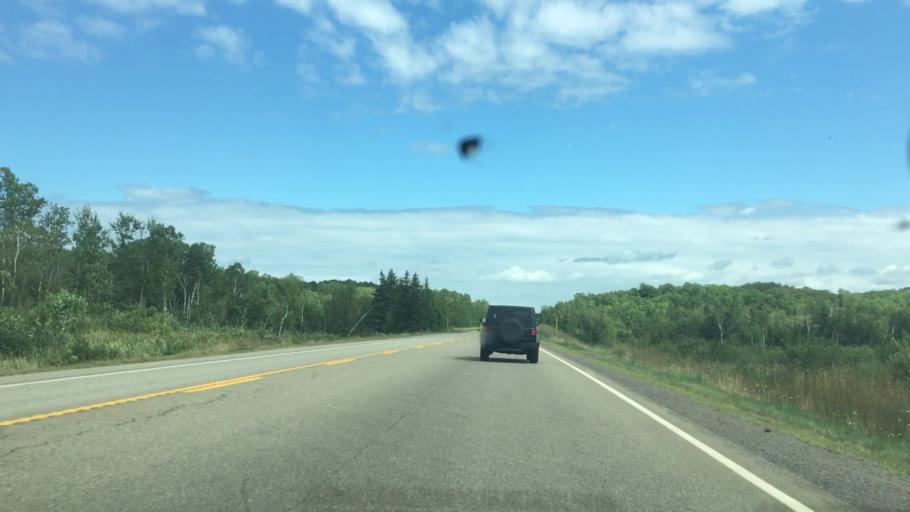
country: CA
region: Nova Scotia
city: Port Hawkesbury
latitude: 45.6260
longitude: -61.5998
